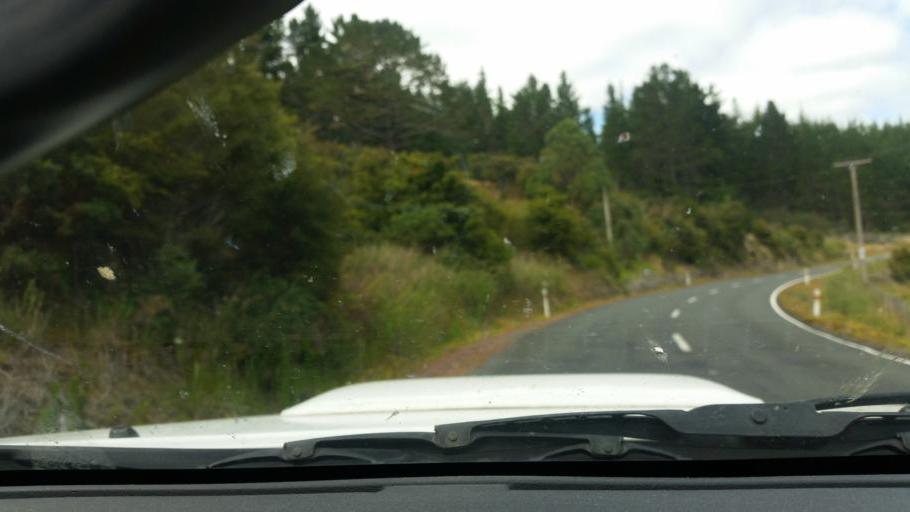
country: NZ
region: Northland
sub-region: Kaipara District
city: Dargaville
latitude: -35.8157
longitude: 173.7262
